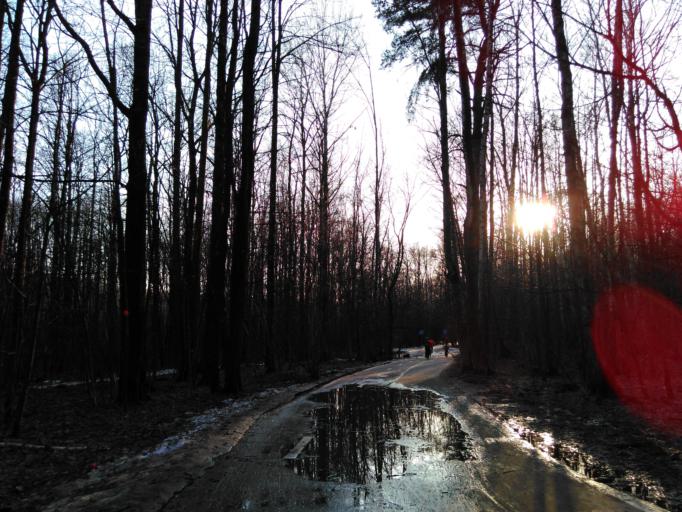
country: RU
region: Moscow
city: Zyuzino
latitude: 55.6324
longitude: 37.5682
